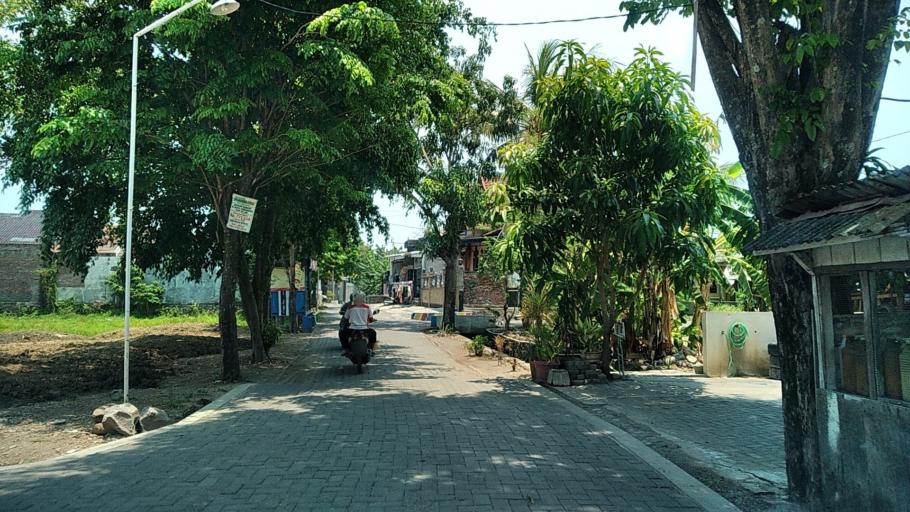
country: ID
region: Central Java
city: Semarang
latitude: -6.9809
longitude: 110.4776
